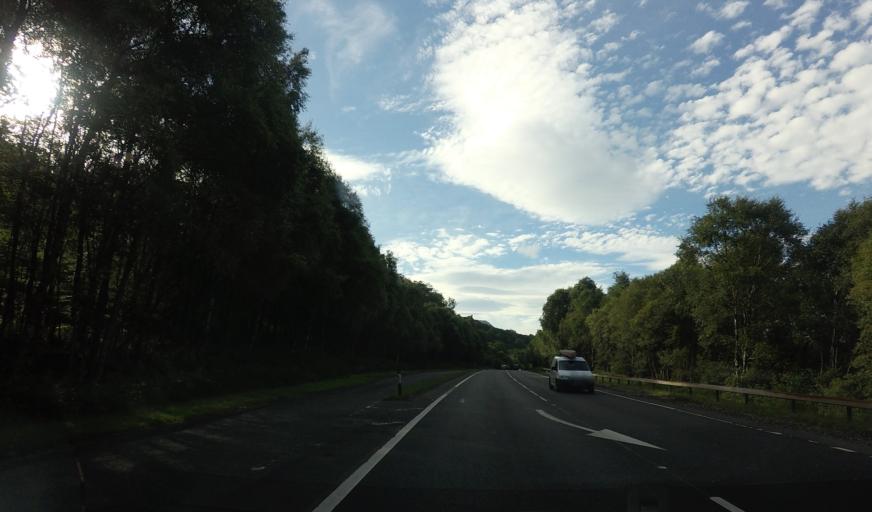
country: GB
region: Scotland
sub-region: Argyll and Bute
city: Helensburgh
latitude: 56.1716
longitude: -4.6811
